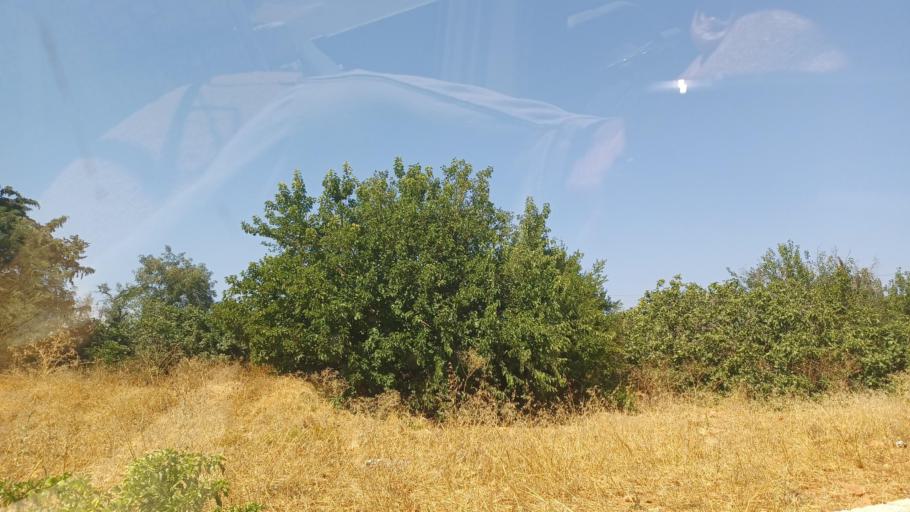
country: CY
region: Pafos
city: Pegeia
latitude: 34.9588
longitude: 32.4002
